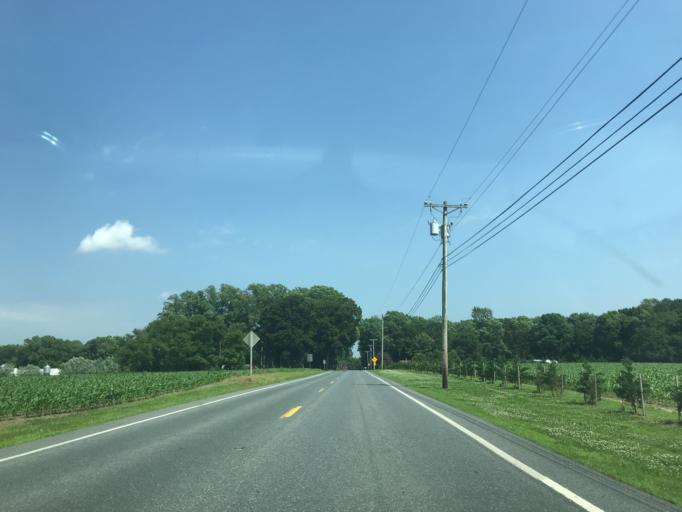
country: US
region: Maryland
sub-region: Dorchester County
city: Hurlock
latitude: 38.5835
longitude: -75.7868
